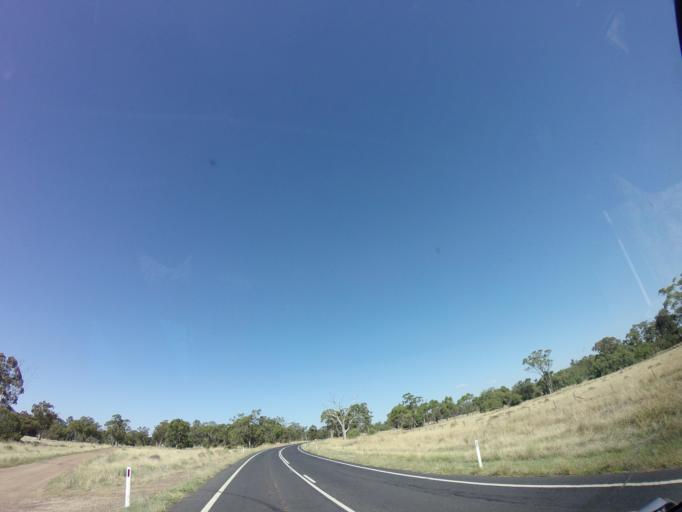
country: AU
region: New South Wales
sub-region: Narromine
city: Narromine
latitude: -31.6419
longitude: 147.9060
